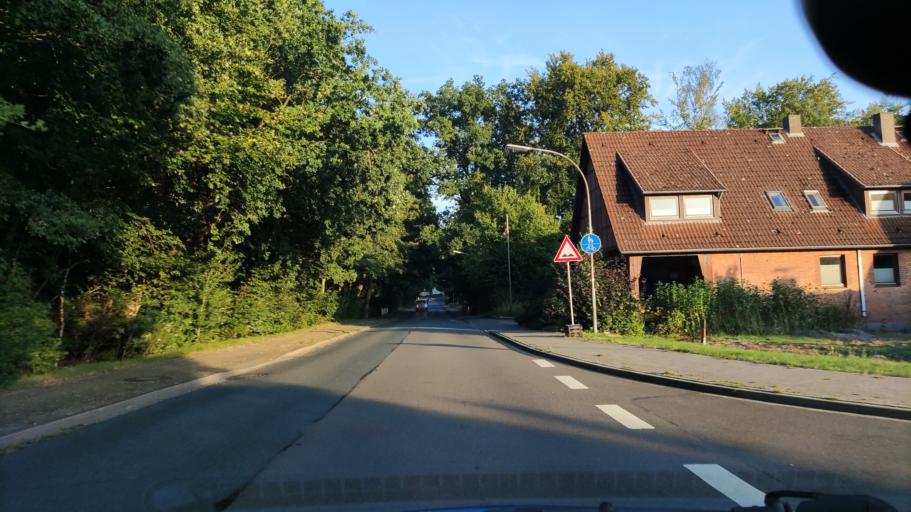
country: DE
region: Lower Saxony
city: Fassberg
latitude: 52.9631
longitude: 10.1795
